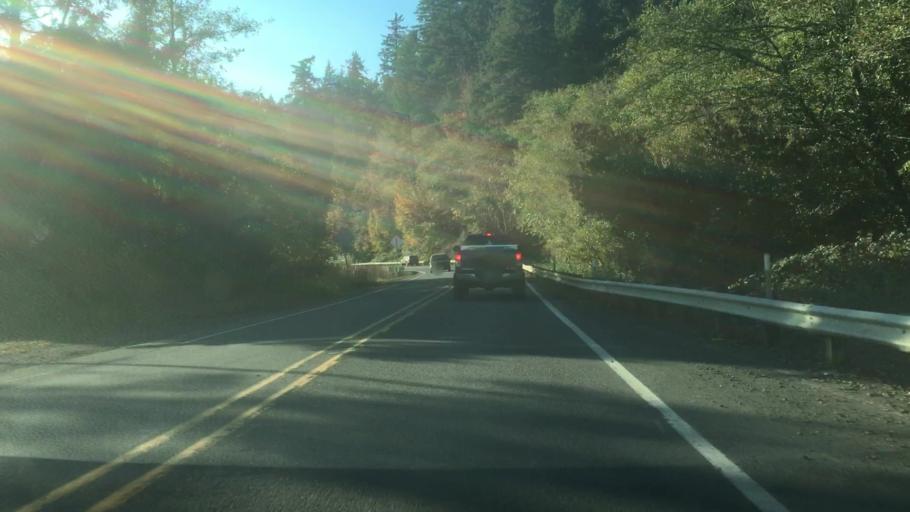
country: US
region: Oregon
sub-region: Clatsop County
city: Astoria
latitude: 46.2491
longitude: -123.8629
